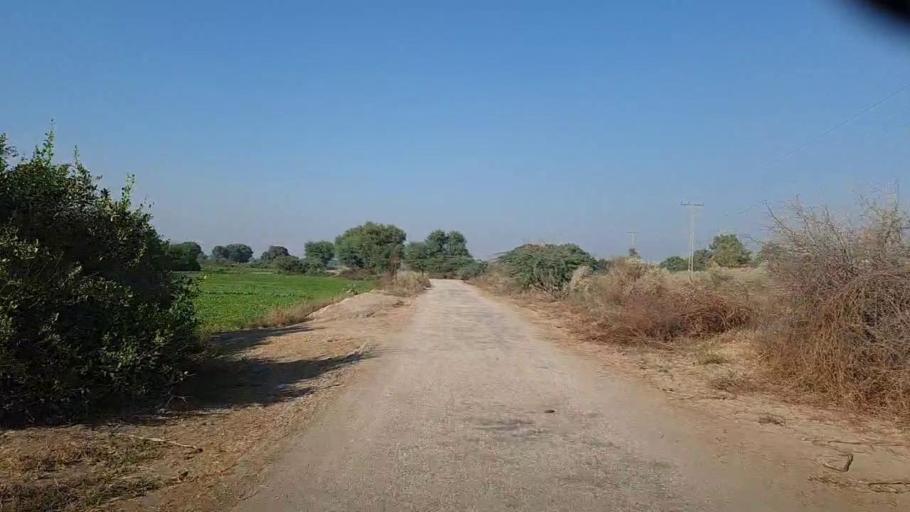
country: PK
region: Sindh
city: Darya Khan Marri
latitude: 26.6807
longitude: 68.3517
